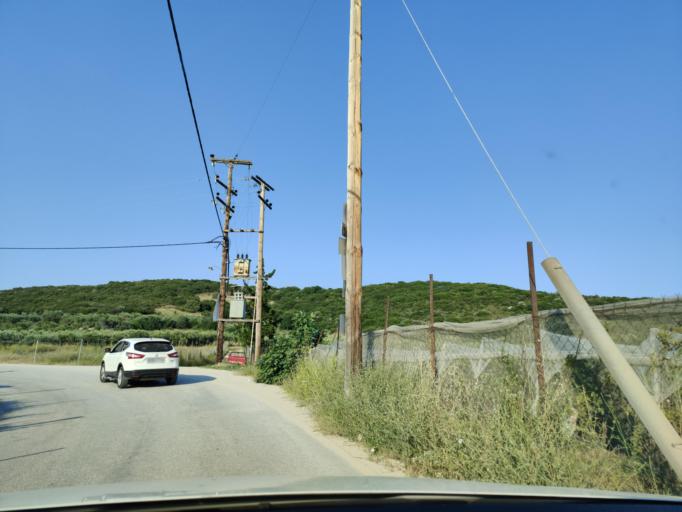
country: GR
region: East Macedonia and Thrace
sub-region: Nomos Kavalas
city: Nea Peramos
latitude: 40.8198
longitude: 24.3076
